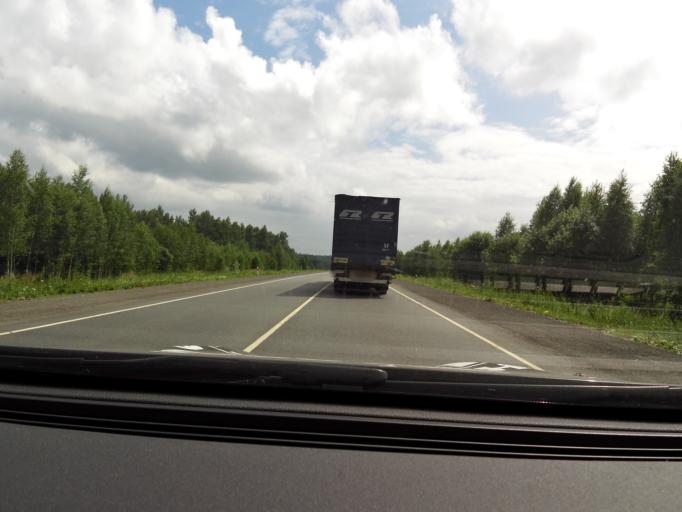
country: RU
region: Perm
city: Ust'-Kishert'
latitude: 57.1653
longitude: 57.1526
